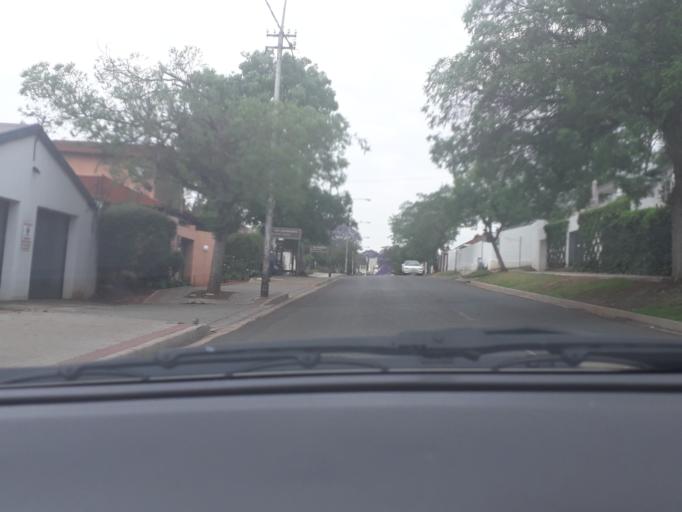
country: ZA
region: Gauteng
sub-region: City of Johannesburg Metropolitan Municipality
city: Johannesburg
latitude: -26.1758
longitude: 27.9975
